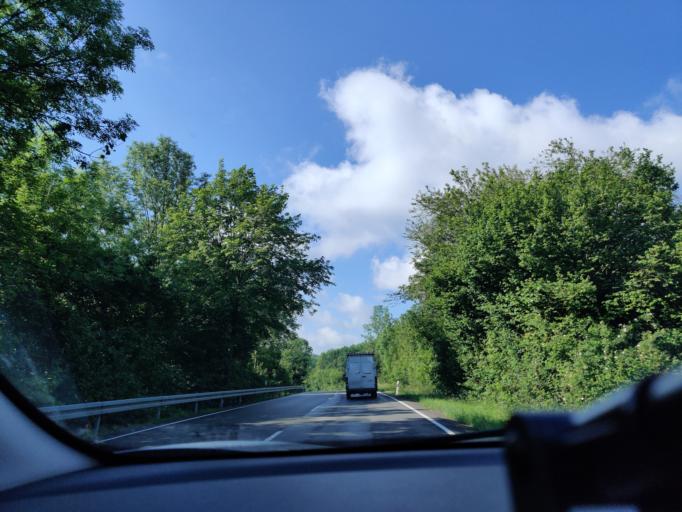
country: FR
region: Lorraine
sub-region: Departement de la Moselle
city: Bliesbruck
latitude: 49.1503
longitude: 7.1530
